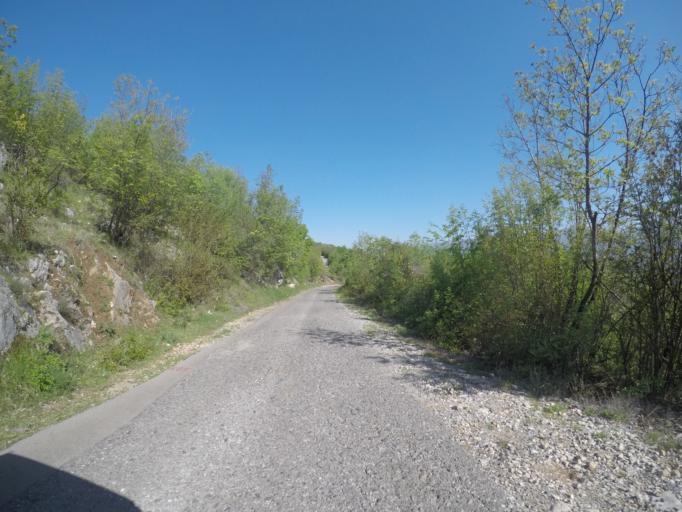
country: ME
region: Danilovgrad
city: Danilovgrad
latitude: 42.5222
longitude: 19.0949
